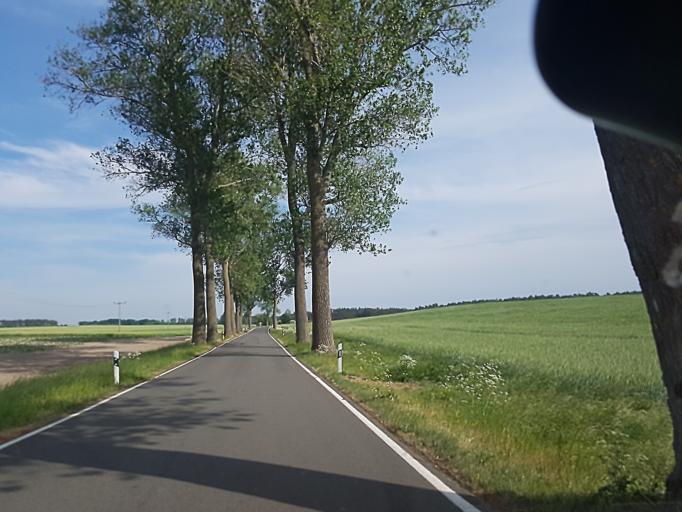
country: DE
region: Saxony-Anhalt
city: Kropstadt
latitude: 51.9782
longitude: 12.7208
